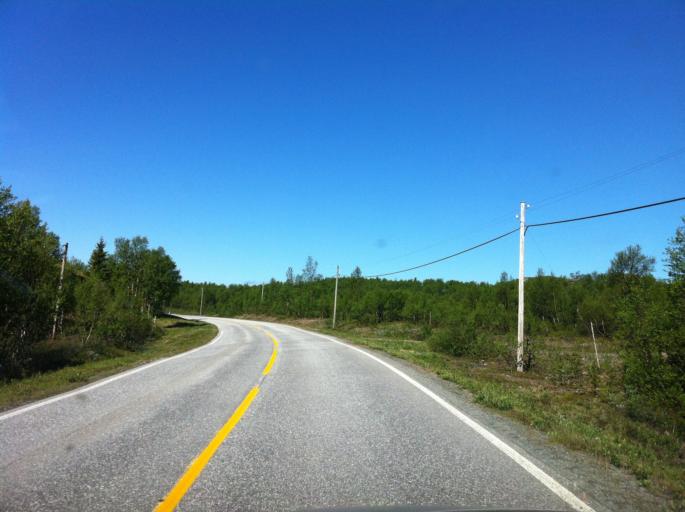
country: NO
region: Sor-Trondelag
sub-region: Tydal
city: Aas
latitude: 62.6409
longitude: 12.0206
